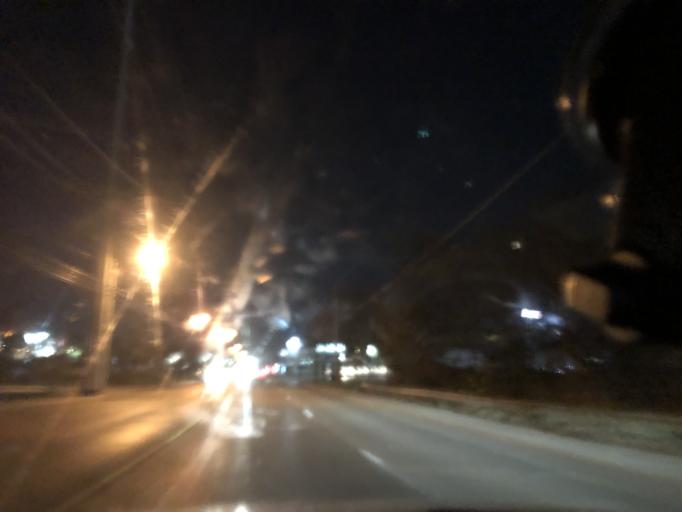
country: US
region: Texas
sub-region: Dallas County
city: University Park
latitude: 32.8220
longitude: -96.8373
